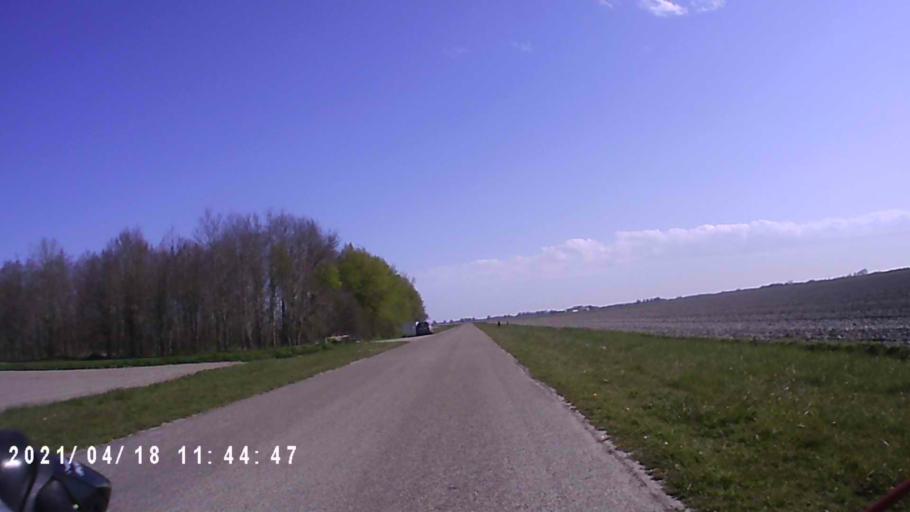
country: NL
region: Groningen
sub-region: Gemeente Zuidhorn
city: Grijpskerk
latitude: 53.3208
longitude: 6.2589
